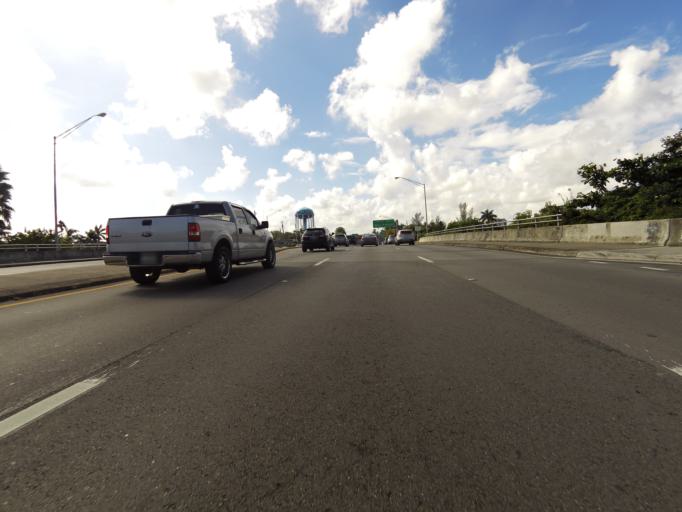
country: US
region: Florida
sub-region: Broward County
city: Hollywood
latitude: 26.0334
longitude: -80.1611
